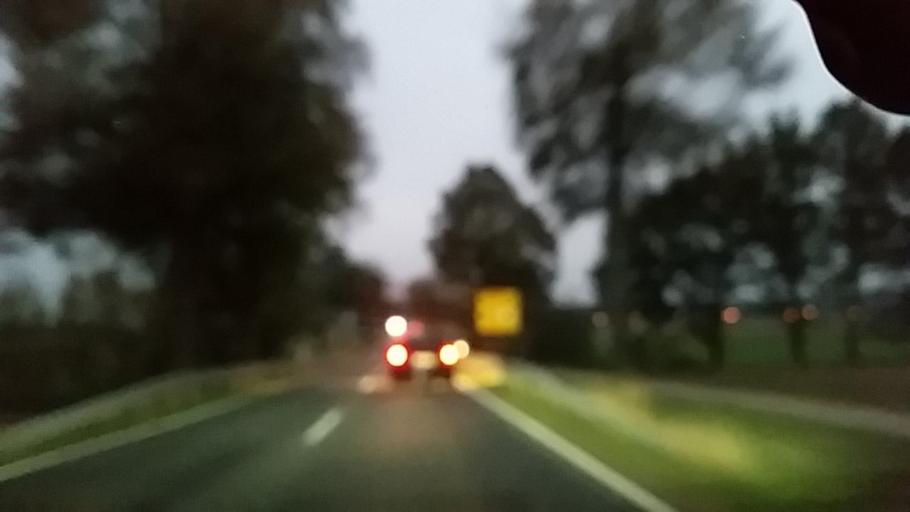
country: DE
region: Lower Saxony
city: Bodenteich
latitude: 52.8527
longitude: 10.6819
